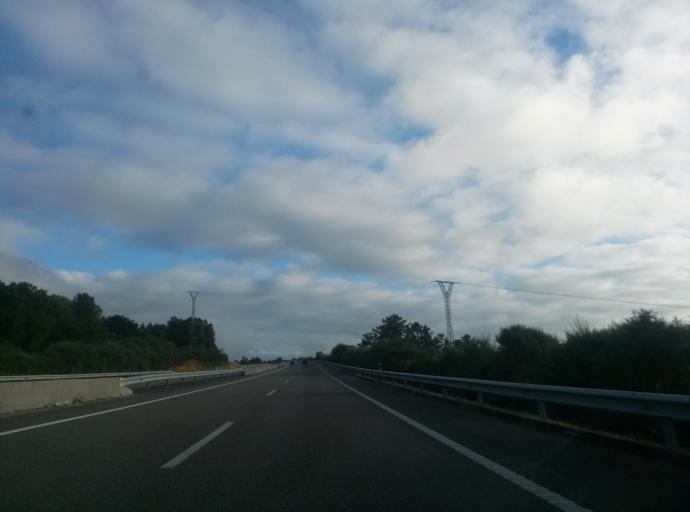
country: ES
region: Galicia
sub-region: Provincia de Lugo
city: Muras
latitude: 43.3757
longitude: -7.7782
